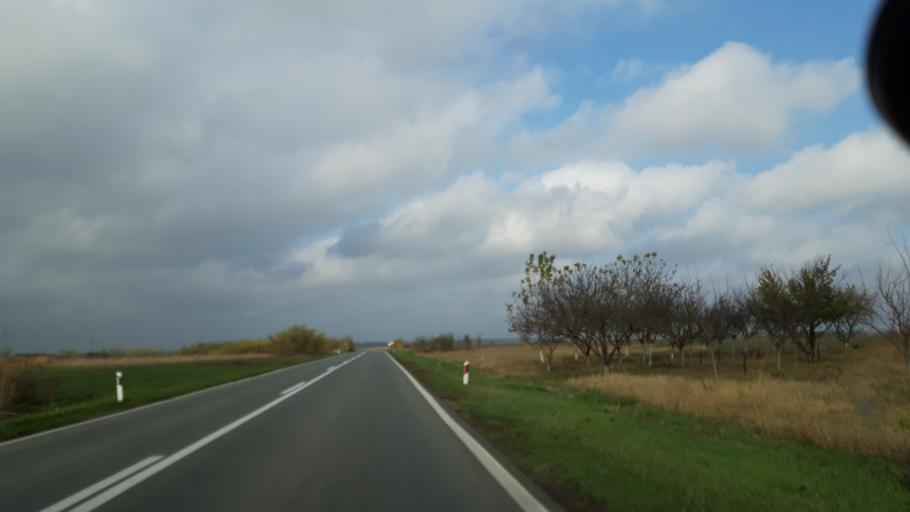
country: RS
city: Ostojicevo
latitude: 45.9014
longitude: 20.1553
